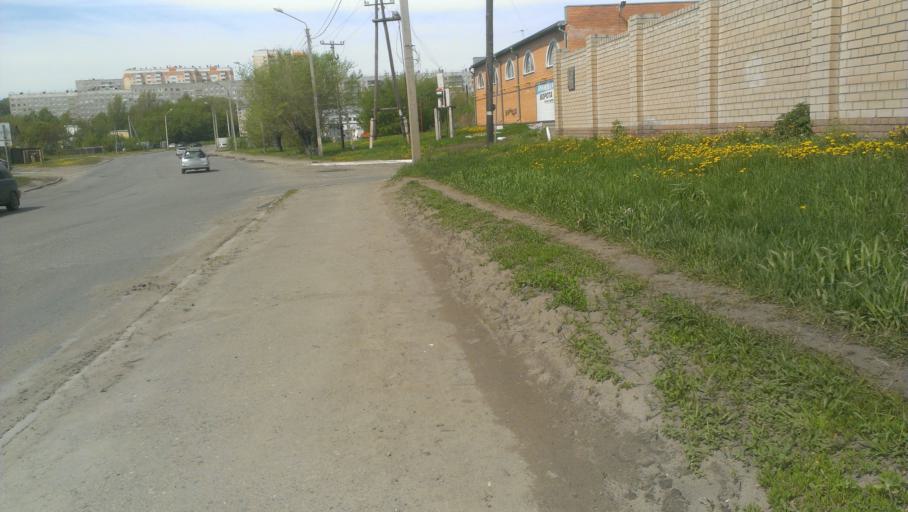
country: RU
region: Altai Krai
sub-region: Gorod Barnaulskiy
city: Barnaul
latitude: 53.3806
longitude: 83.6883
